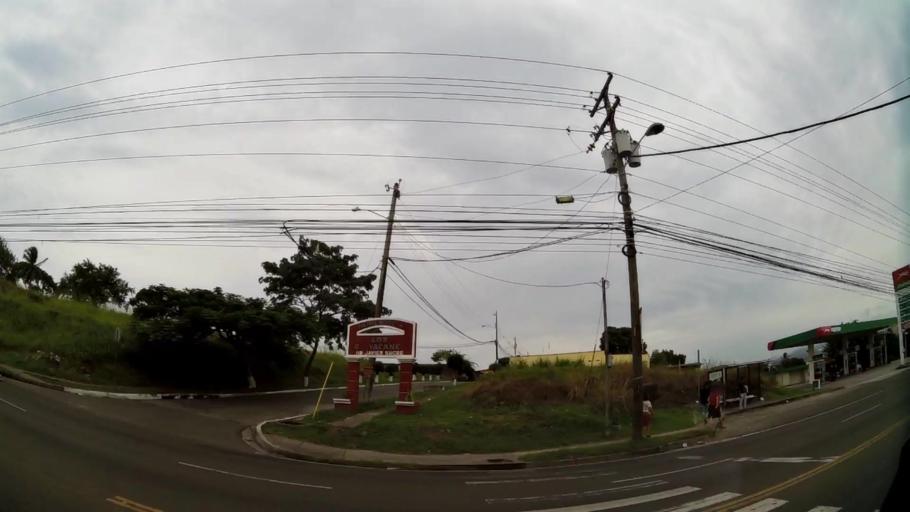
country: PA
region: Panama
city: San Miguelito
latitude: 9.0434
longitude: -79.4553
